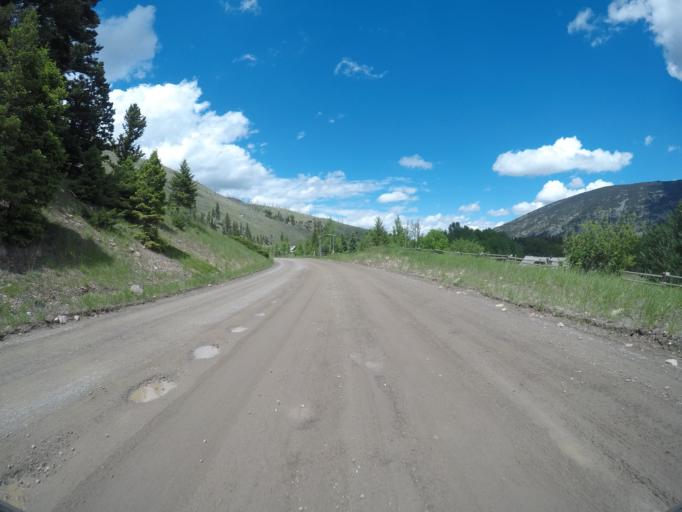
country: US
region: Montana
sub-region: Park County
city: Livingston
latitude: 45.5439
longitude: -110.2149
